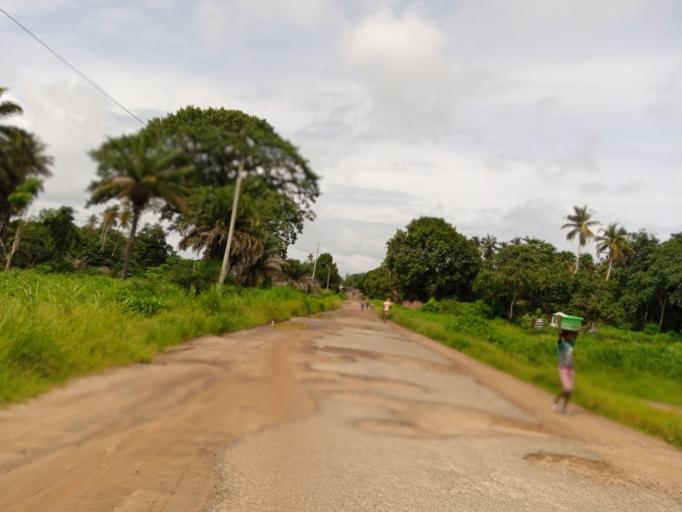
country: SL
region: Northern Province
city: Masoyila
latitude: 8.5915
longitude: -13.1983
